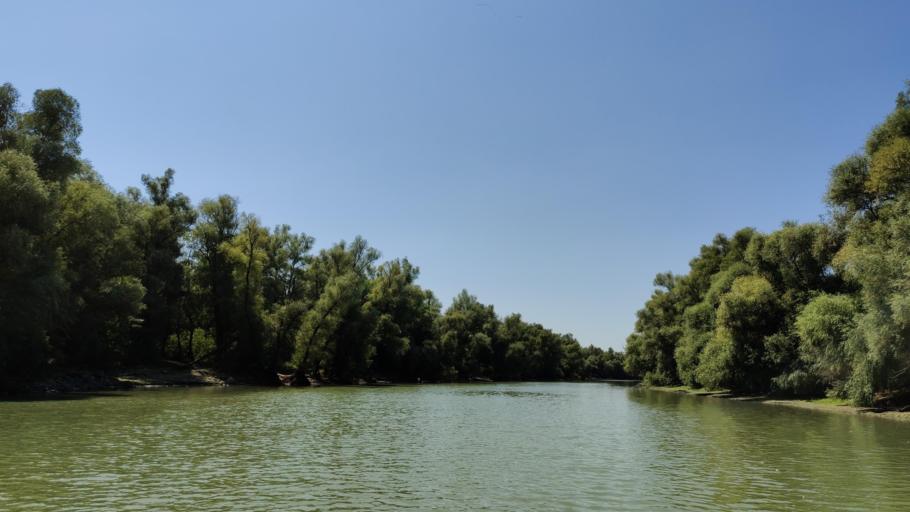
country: RO
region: Tulcea
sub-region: Comuna Nufaru
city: Nufaru
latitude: 45.2332
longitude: 28.9114
